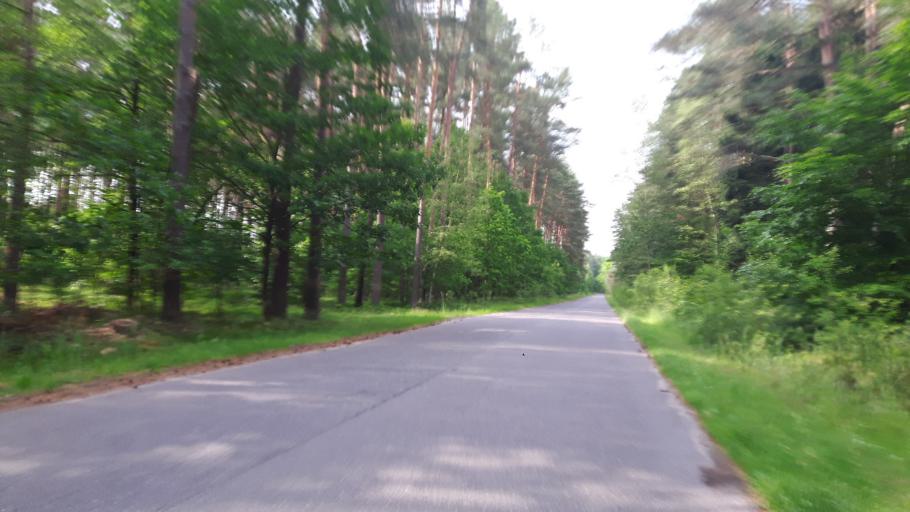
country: PL
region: West Pomeranian Voivodeship
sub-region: Powiat goleniowski
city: Nowogard
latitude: 53.7993
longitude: 15.1277
